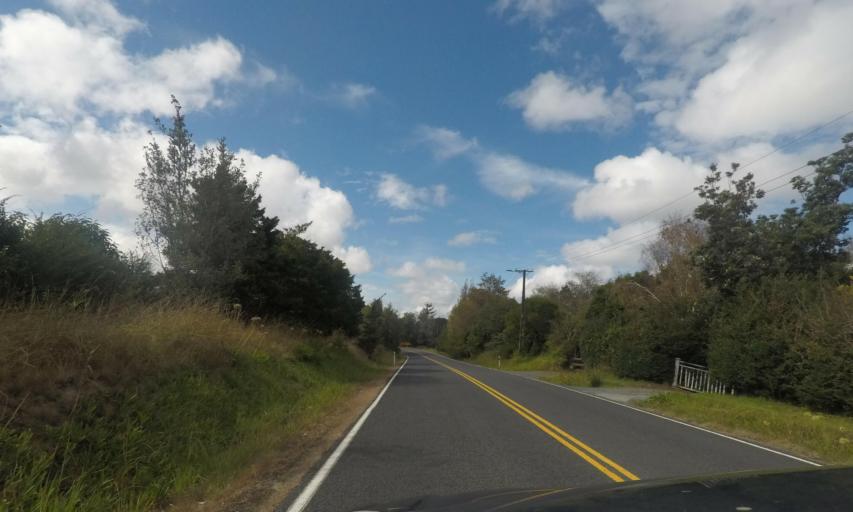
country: NZ
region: Auckland
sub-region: Auckland
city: Rosebank
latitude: -36.7981
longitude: 174.6350
